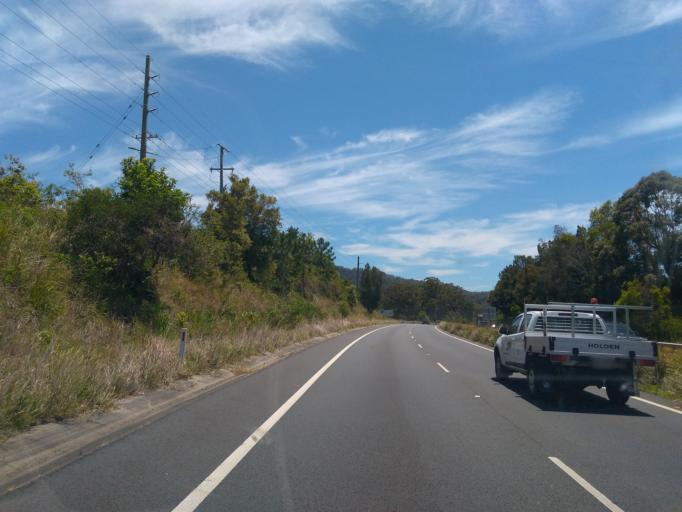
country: AU
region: New South Wales
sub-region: Coffs Harbour
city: Coffs Harbour
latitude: -30.2590
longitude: 153.1284
